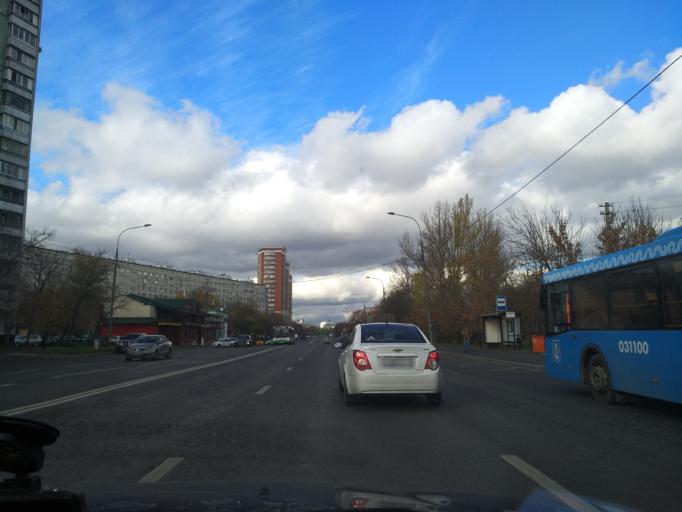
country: RU
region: Moscow
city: Kozeyevo
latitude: 55.8701
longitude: 37.6205
